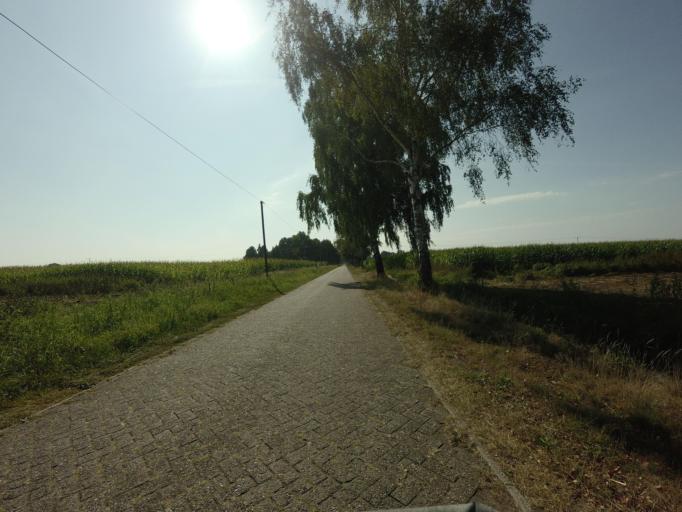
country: DE
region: Lower Saxony
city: Emlichheim
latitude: 52.5939
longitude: 6.8332
